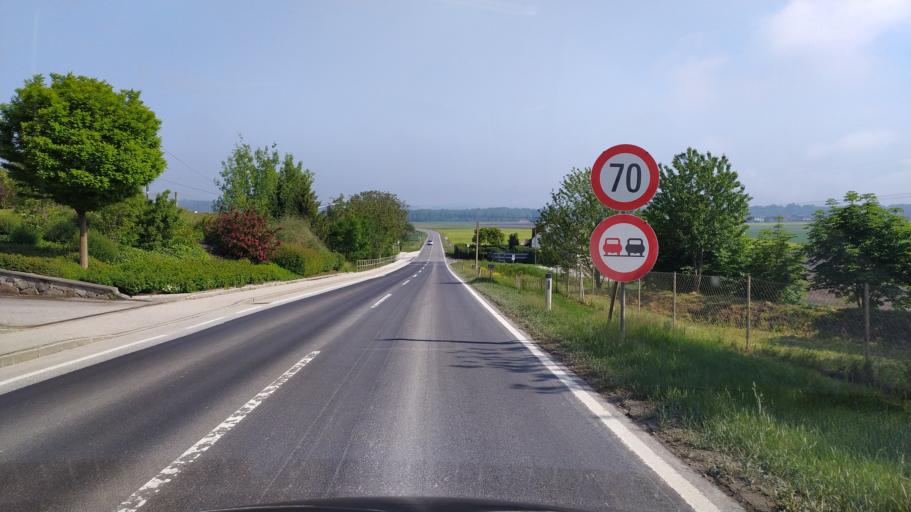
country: AT
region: Lower Austria
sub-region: Politischer Bezirk Amstetten
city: Ennsdorf
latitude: 48.2172
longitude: 14.5396
